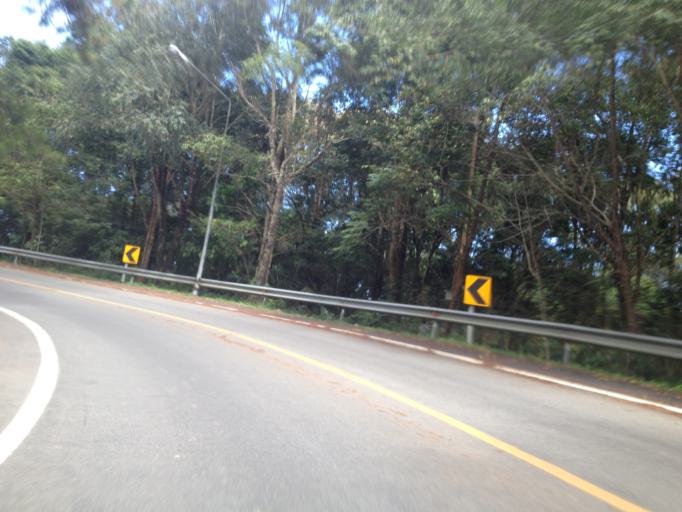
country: TH
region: Chiang Mai
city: Chiang Mai
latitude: 18.8018
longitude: 98.9035
